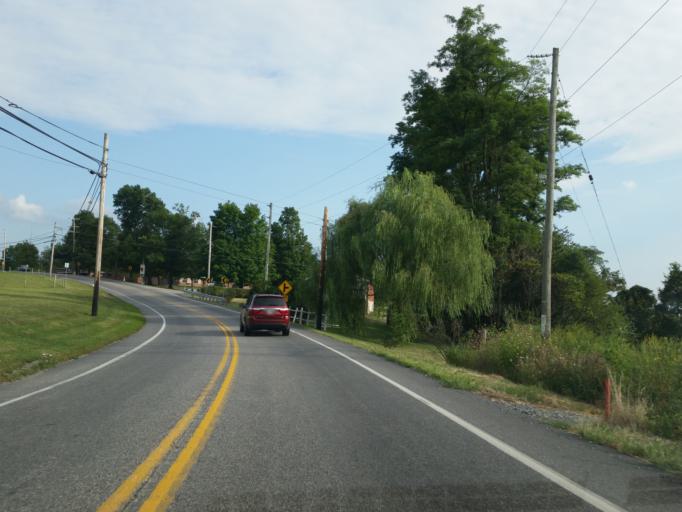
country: US
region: Pennsylvania
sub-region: Lebanon County
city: Annville
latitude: 40.3533
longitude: -76.5456
